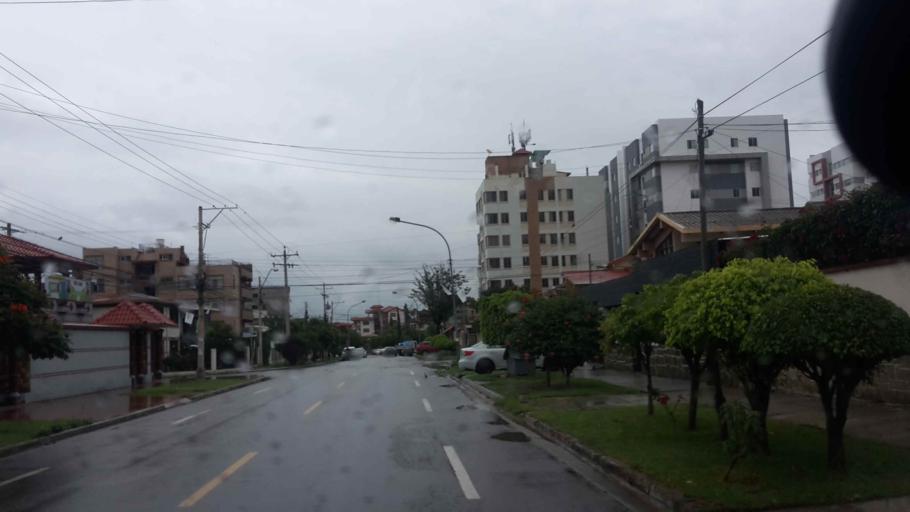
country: BO
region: Cochabamba
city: Cochabamba
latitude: -17.3758
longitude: -66.1649
